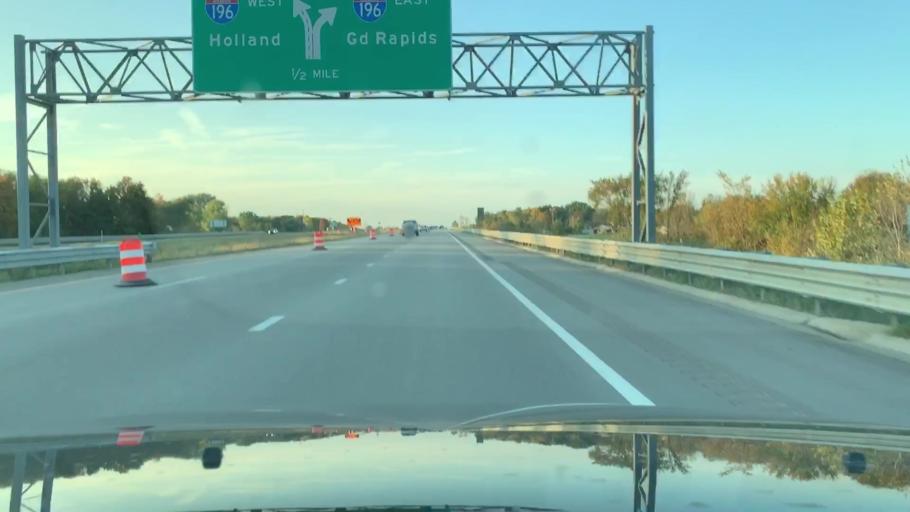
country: US
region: Michigan
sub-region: Ottawa County
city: Hudsonville
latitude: 42.8520
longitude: -85.8101
